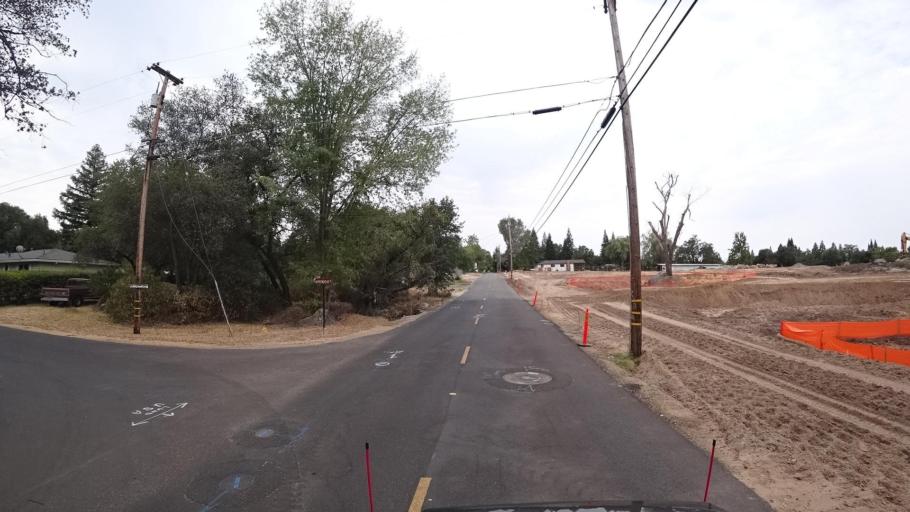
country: US
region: California
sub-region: Placer County
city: Rocklin
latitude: 38.7837
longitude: -121.2197
